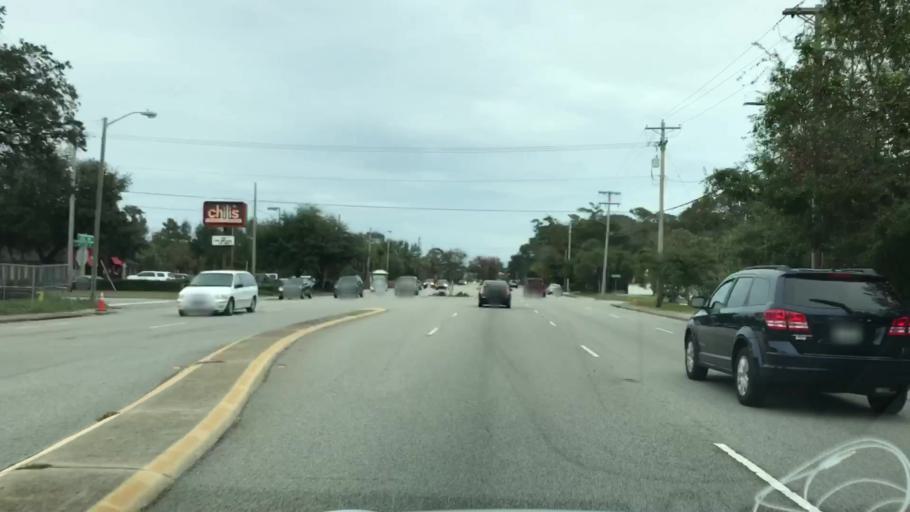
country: US
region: South Carolina
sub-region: Horry County
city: Myrtle Beach
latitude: 33.7191
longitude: -78.8520
